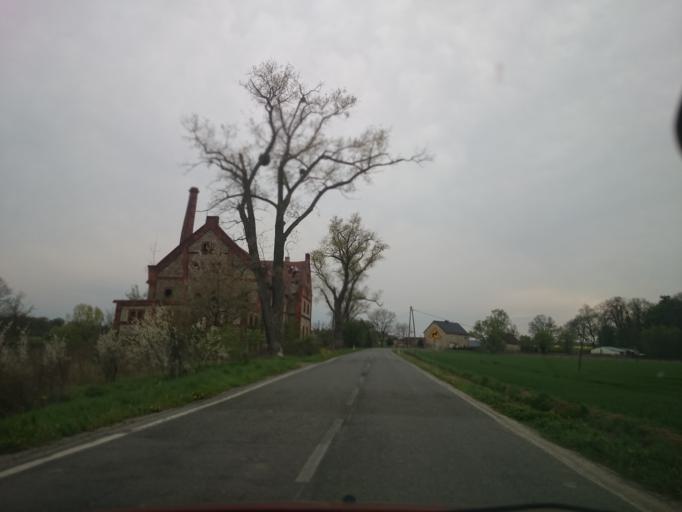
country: PL
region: Lower Silesian Voivodeship
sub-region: Powiat strzelinski
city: Przeworno
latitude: 50.6474
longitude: 17.1691
